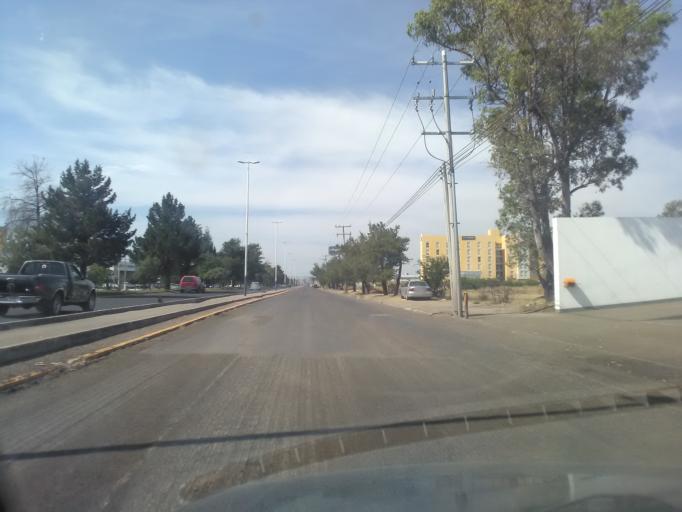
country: MX
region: Durango
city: Victoria de Durango
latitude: 24.0542
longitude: -104.6160
